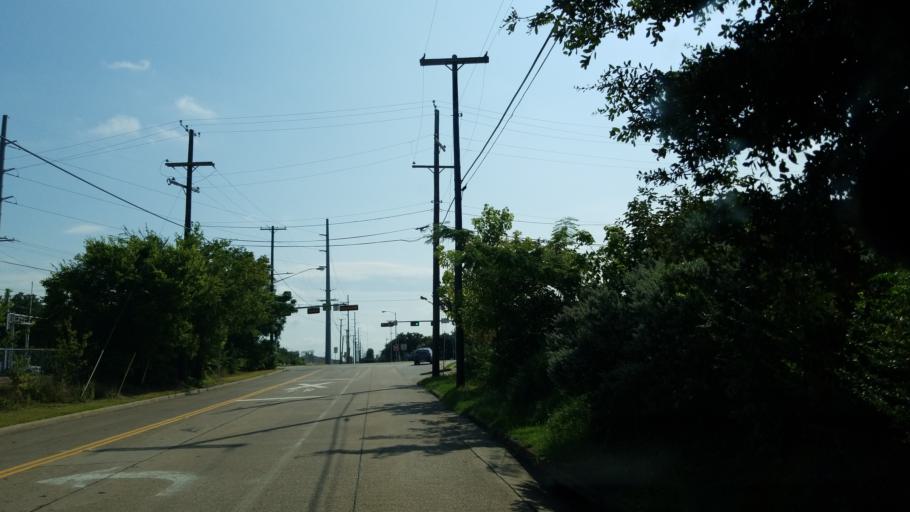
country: US
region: Texas
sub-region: Dallas County
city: Garland
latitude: 32.9138
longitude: -96.6490
